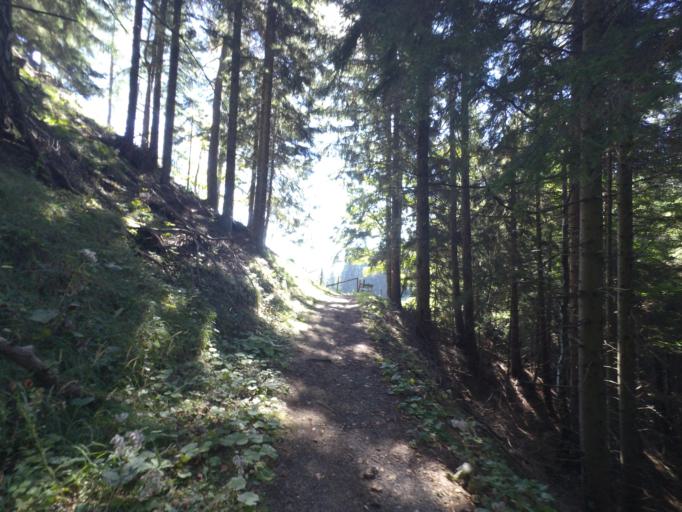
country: AT
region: Styria
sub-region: Politischer Bezirk Weiz
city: Passail
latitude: 47.3317
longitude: 15.4640
